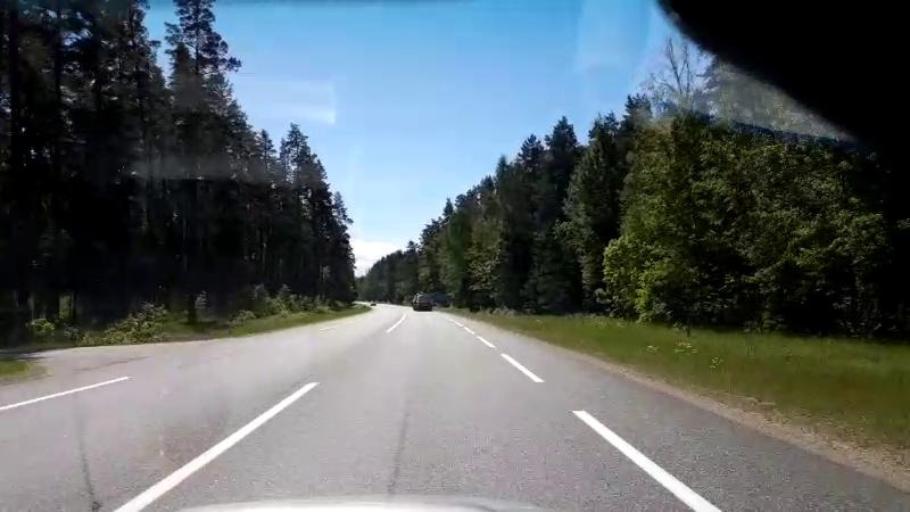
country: LV
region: Saulkrastu
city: Saulkrasti
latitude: 57.3970
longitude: 24.4280
